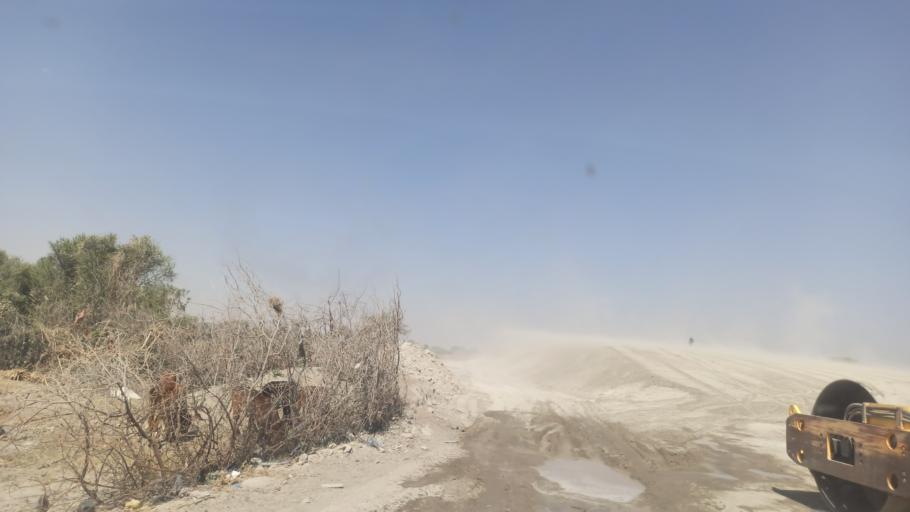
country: ET
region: Oromiya
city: Ziway
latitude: 7.6973
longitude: 38.6442
